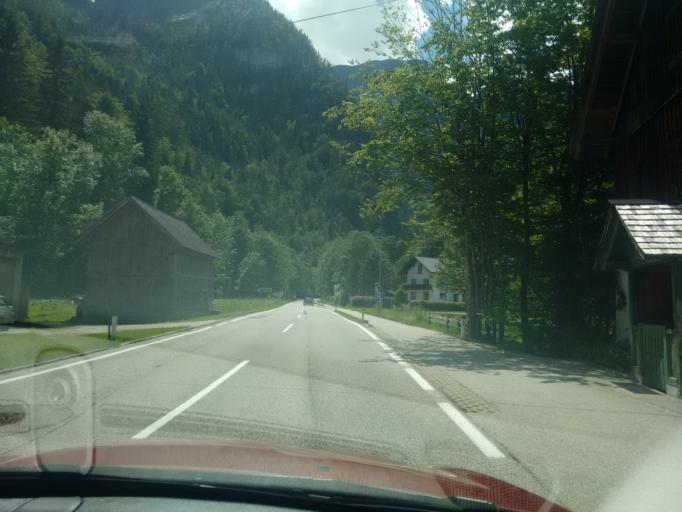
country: AT
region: Upper Austria
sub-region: Politischer Bezirk Gmunden
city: Bad Goisern
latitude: 47.5495
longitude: 13.6788
